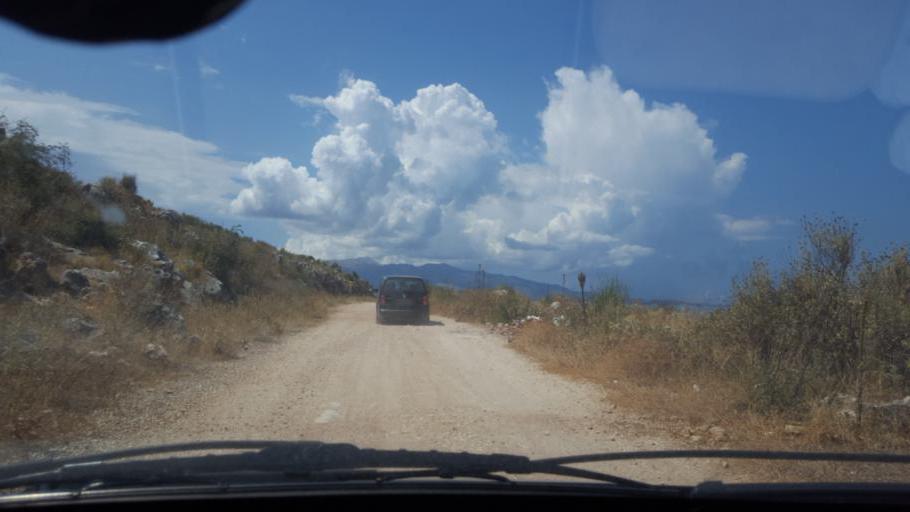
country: AL
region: Vlore
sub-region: Rrethi i Sarandes
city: Sarande
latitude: 39.8425
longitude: 20.0161
